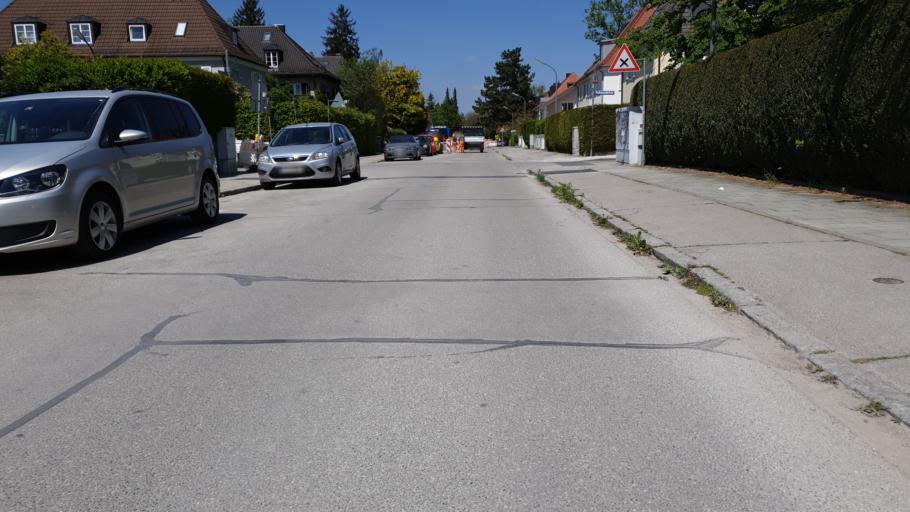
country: DE
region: Bavaria
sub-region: Upper Bavaria
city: Pasing
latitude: 48.1512
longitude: 11.4688
